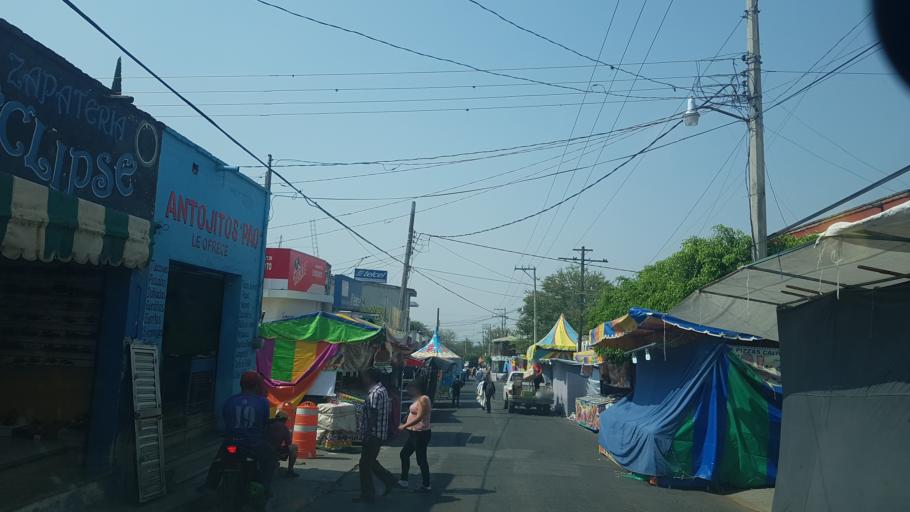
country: MX
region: Morelos
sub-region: Temoac
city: Temoac
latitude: 18.7722
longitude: -98.7780
